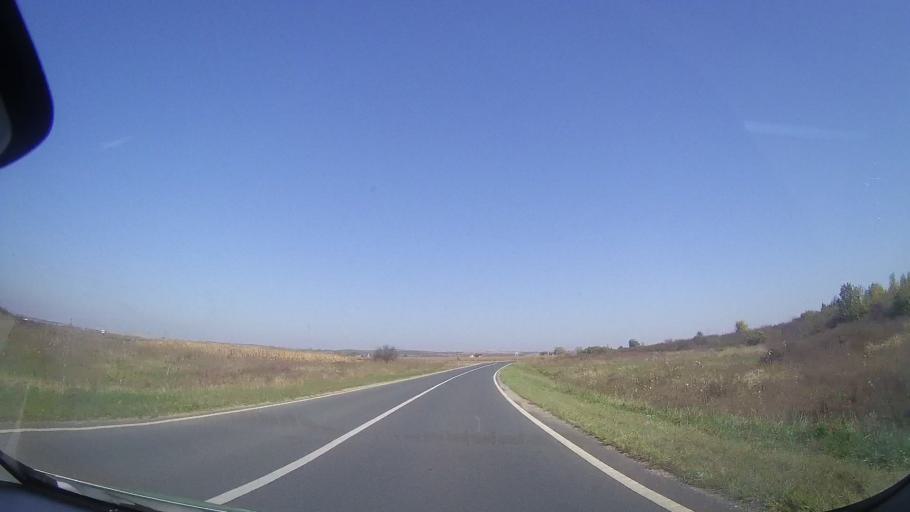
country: RO
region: Timis
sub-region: Comuna Balint
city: Balint
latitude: 45.7898
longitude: 21.8570
